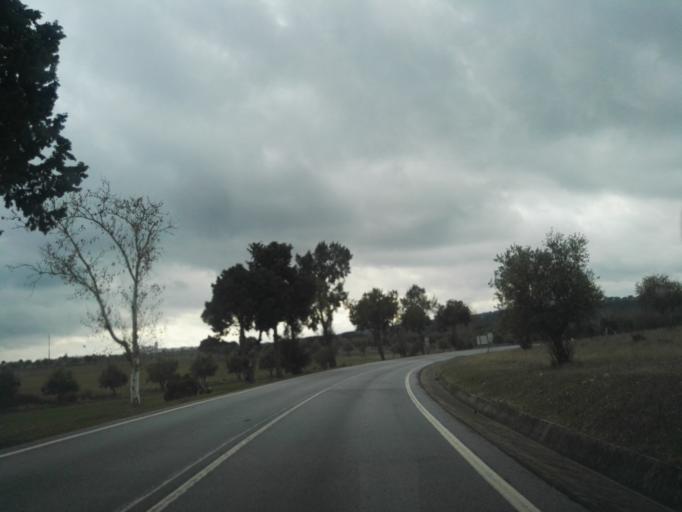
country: PT
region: Portalegre
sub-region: Arronches
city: Arronches
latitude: 39.1337
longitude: -7.2909
